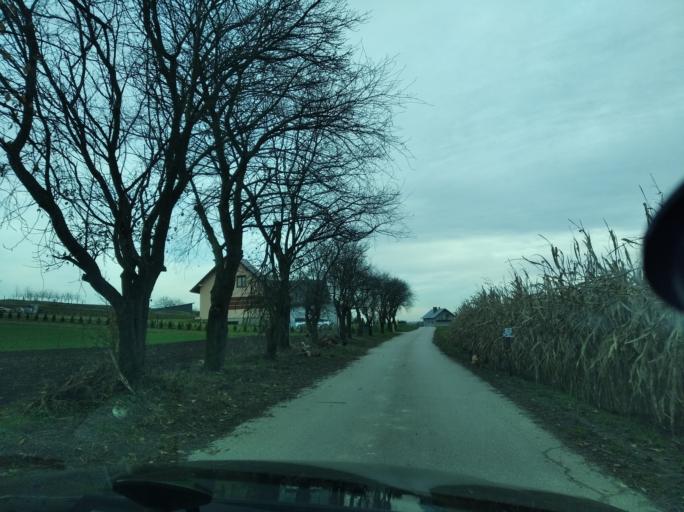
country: PL
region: Subcarpathian Voivodeship
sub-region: Powiat przeworski
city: Debow
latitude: 50.0497
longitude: 22.4233
